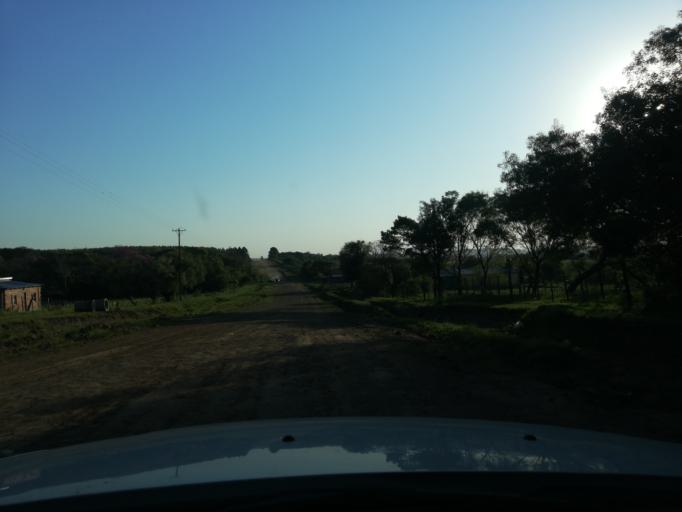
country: AR
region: Misiones
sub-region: Departamento de Apostoles
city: San Jose
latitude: -27.6328
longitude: -55.7331
